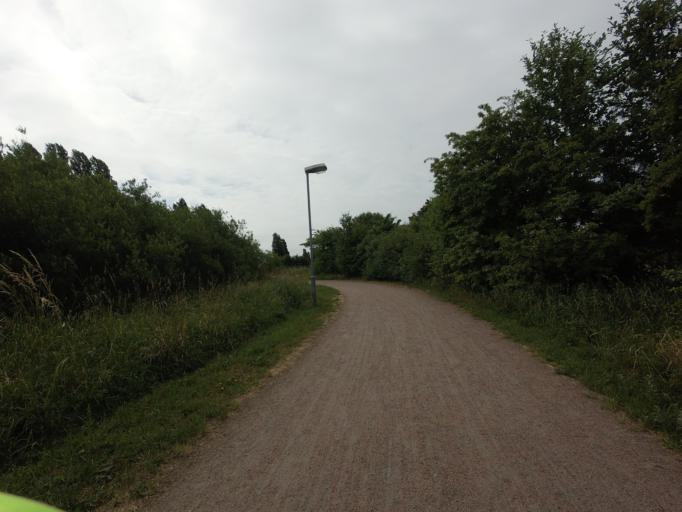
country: SE
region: Skane
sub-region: Malmo
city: Bunkeflostrand
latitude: 55.5571
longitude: 12.9082
